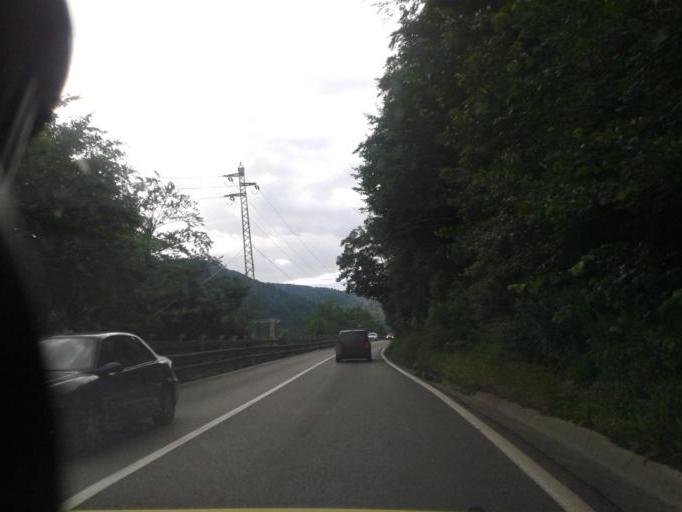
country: RO
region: Prahova
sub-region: Comuna Comarnic
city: Posada
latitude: 45.2944
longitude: 25.6011
